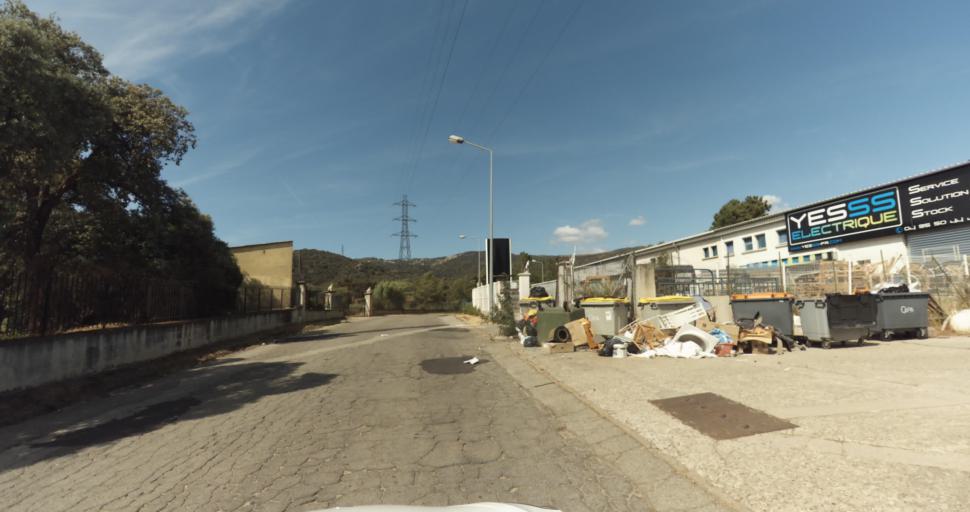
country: FR
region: Corsica
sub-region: Departement de la Corse-du-Sud
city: Ajaccio
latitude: 41.9481
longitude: 8.7631
